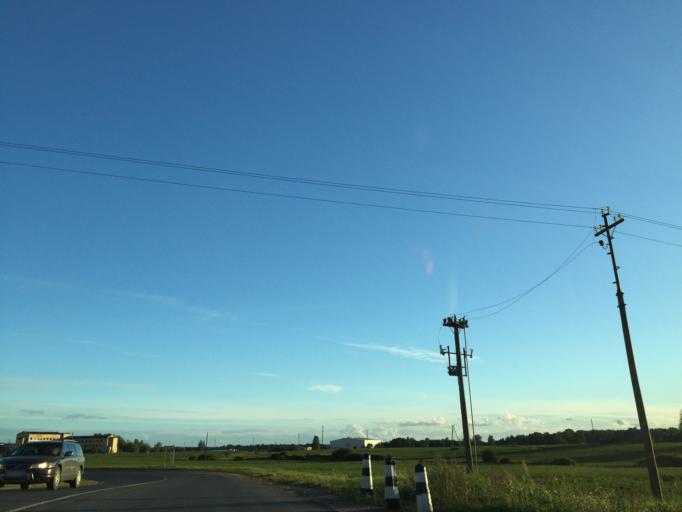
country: LV
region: Saldus Rajons
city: Saldus
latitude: 56.6882
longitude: 22.4587
